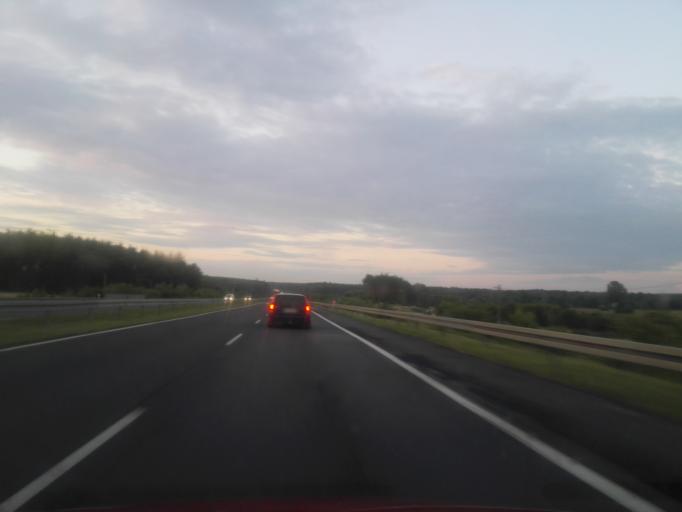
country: PL
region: Lodz Voivodeship
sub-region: Powiat radomszczanski
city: Gomunice
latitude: 51.1507
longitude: 19.4386
